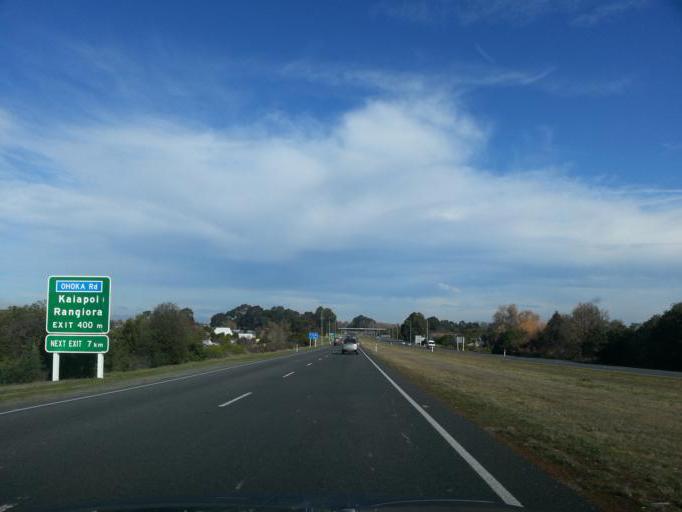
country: NZ
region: Canterbury
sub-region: Waimakariri District
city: Kaiapoi
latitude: -43.3805
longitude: 172.6440
